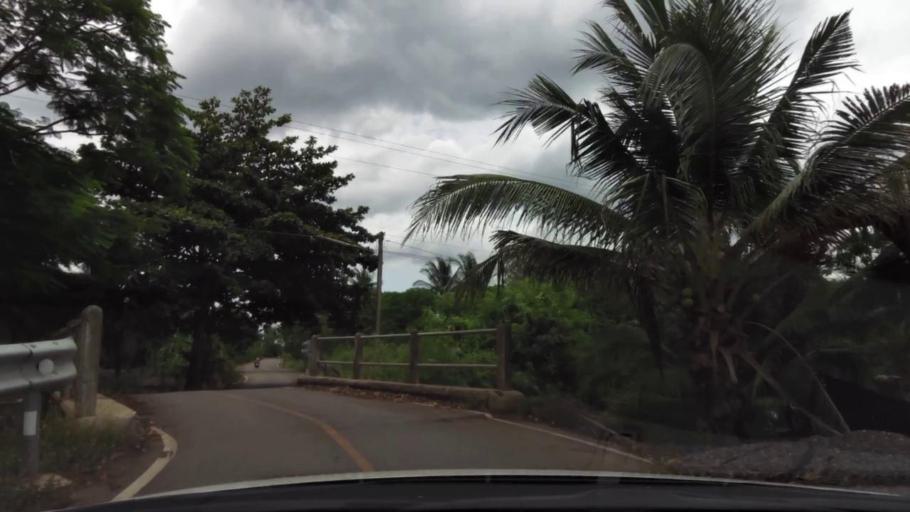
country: TH
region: Samut Sakhon
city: Ban Phaeo
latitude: 13.5619
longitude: 100.0338
